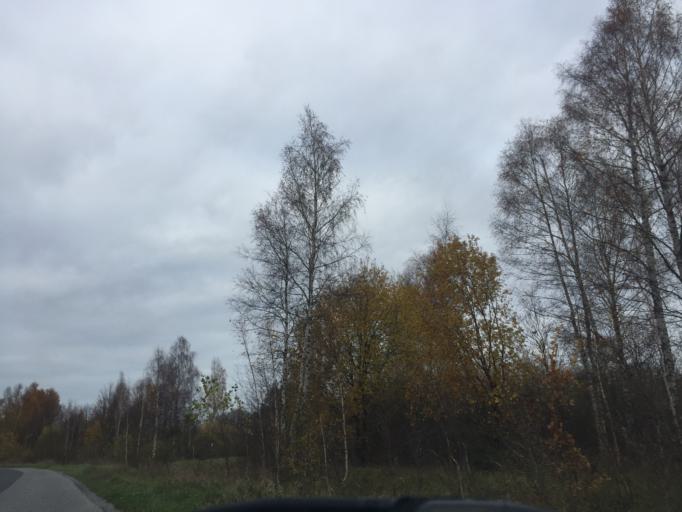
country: LV
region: Liepaja
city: Vec-Liepaja
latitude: 56.5532
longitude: 21.0687
